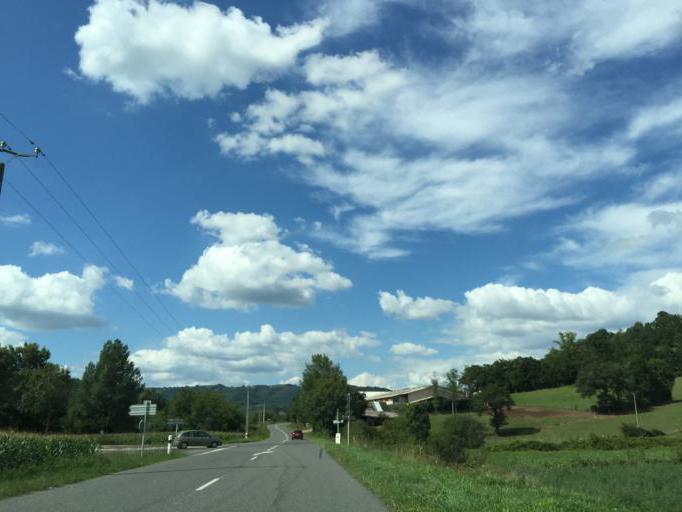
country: FR
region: Midi-Pyrenees
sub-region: Departement de l'Aveyron
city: Saint-Christophe-Vallon
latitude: 44.5328
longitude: 2.4098
